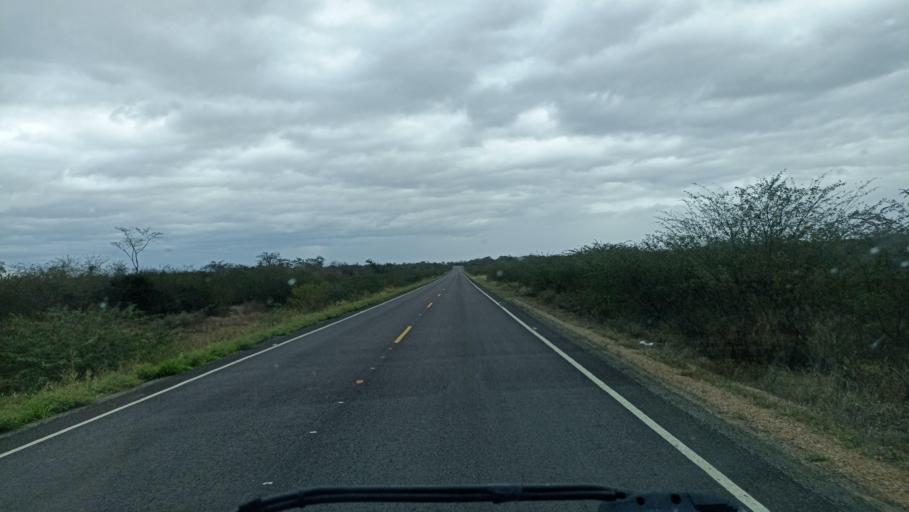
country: BR
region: Bahia
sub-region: Iacu
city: Iacu
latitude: -12.9745
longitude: -40.5092
